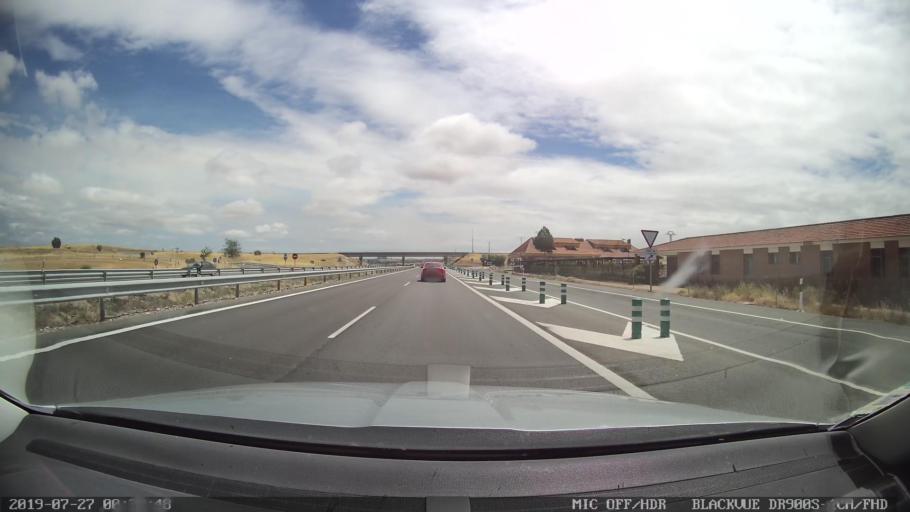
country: ES
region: Castille-La Mancha
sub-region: Province of Toledo
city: Herreruela de Oropesa
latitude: 39.9022
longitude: -5.2464
